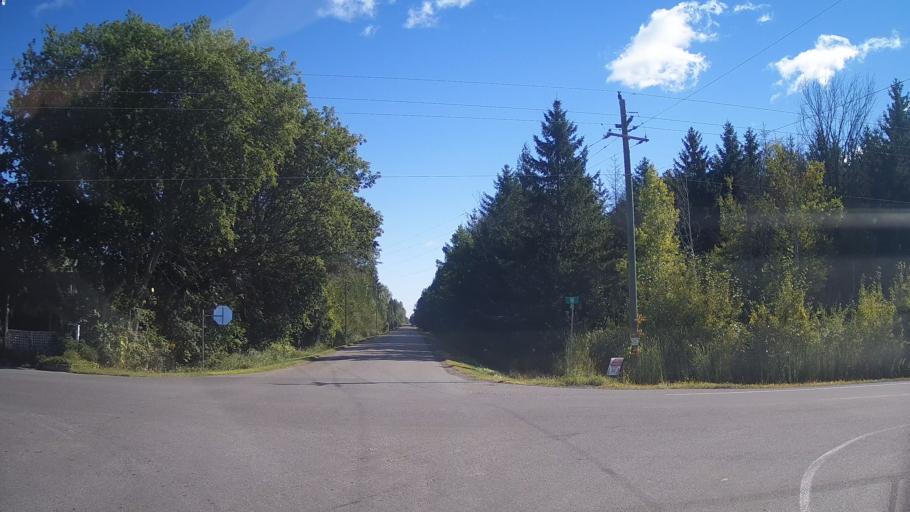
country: CA
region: Ontario
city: Prescott
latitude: 44.9173
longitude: -75.4117
